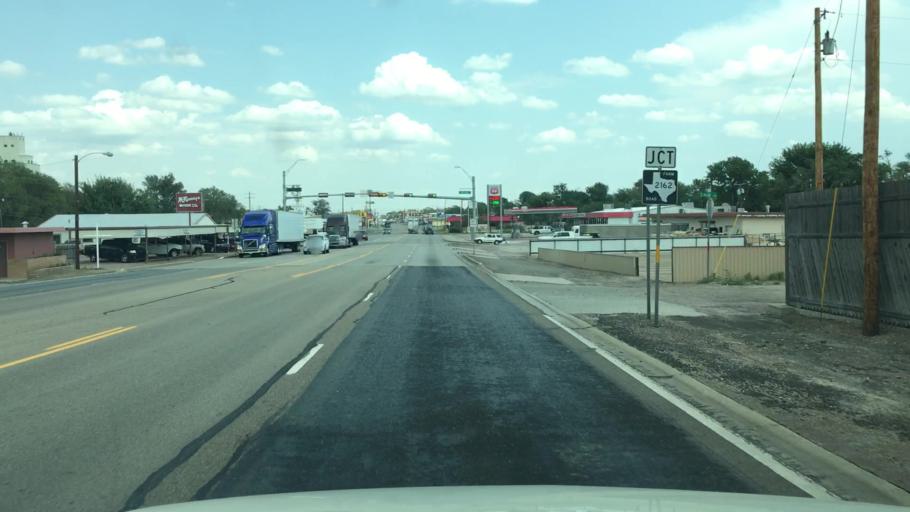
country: US
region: Texas
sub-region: Donley County
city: Clarendon
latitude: 34.9416
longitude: -100.8956
